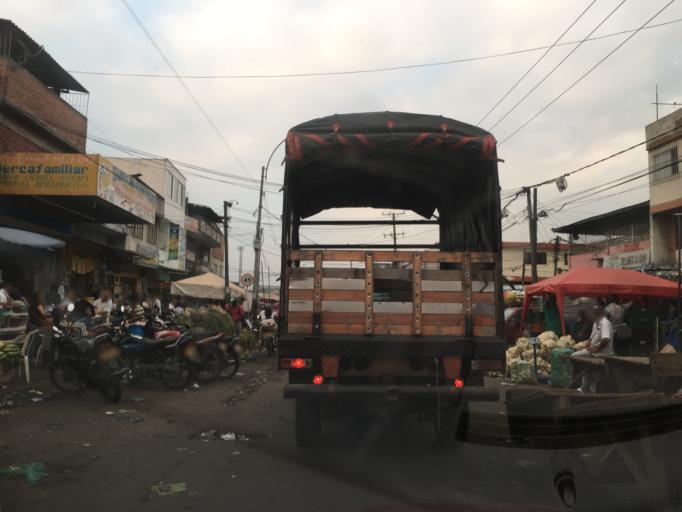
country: CO
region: Valle del Cauca
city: Cali
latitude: 3.4290
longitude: -76.5209
